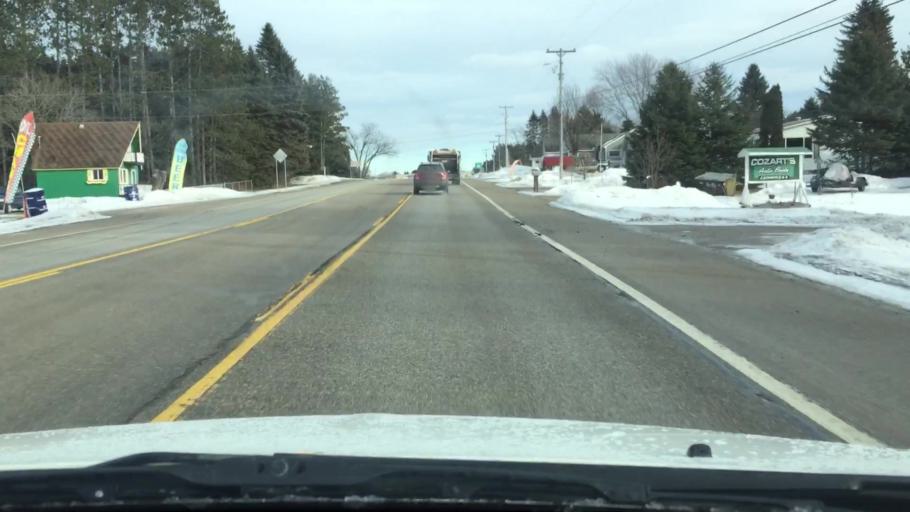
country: US
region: Michigan
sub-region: Wexford County
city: Manton
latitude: 44.4037
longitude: -85.3900
